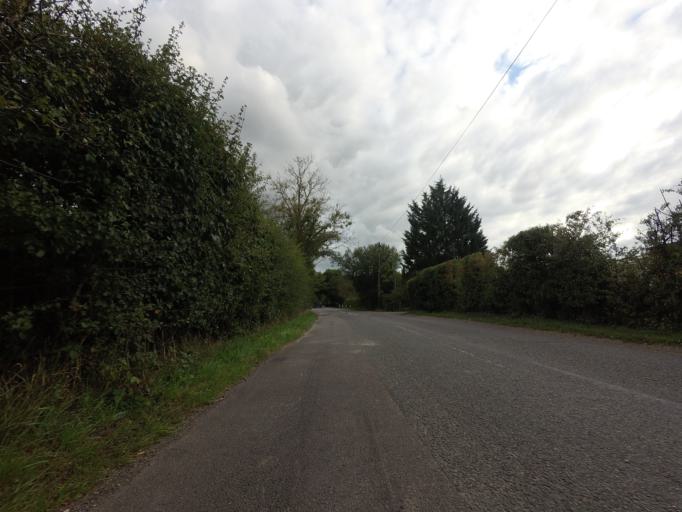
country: GB
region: England
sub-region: Kent
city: Staplehurst
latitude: 51.1812
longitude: 0.5854
